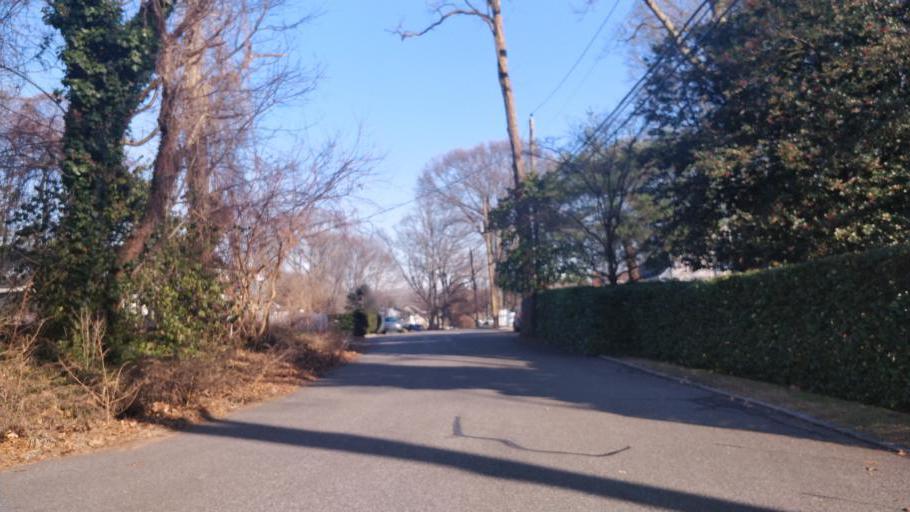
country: US
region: New York
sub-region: Nassau County
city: Bayville
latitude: 40.9060
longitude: -73.5764
